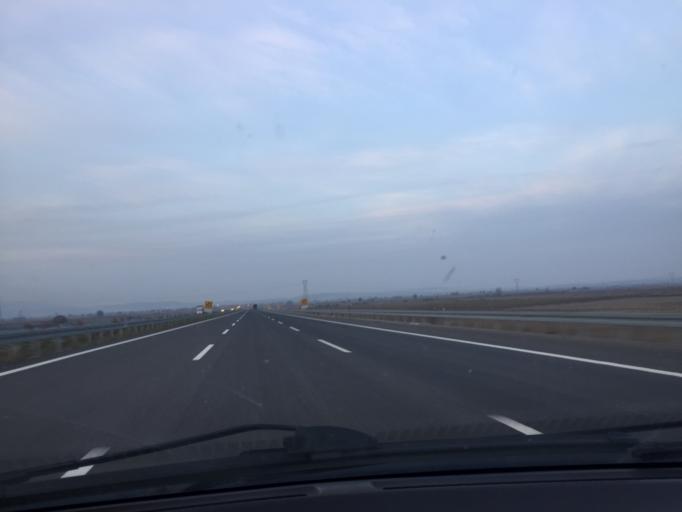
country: TR
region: Manisa
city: Halitpasa
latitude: 38.7123
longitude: 27.6481
